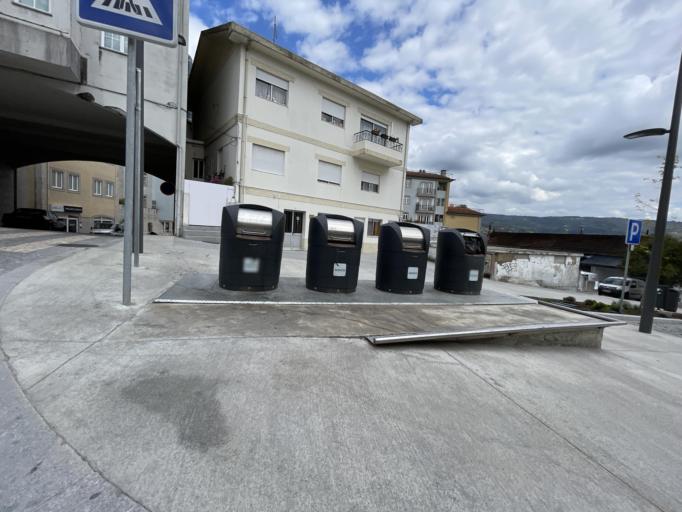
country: PT
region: Porto
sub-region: Marco de Canaveses
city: Marco de Canavezes
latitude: 41.1845
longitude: -8.1471
